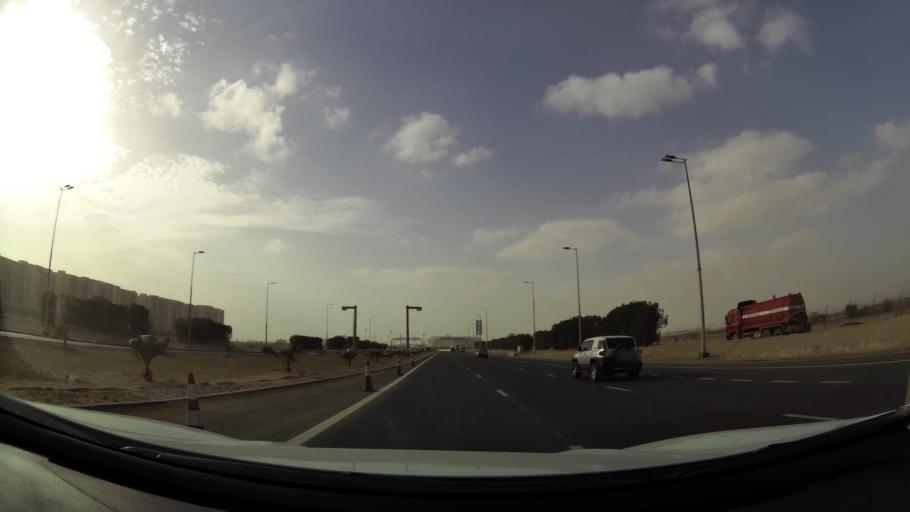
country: AE
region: Abu Dhabi
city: Abu Dhabi
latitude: 24.4589
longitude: 54.6187
